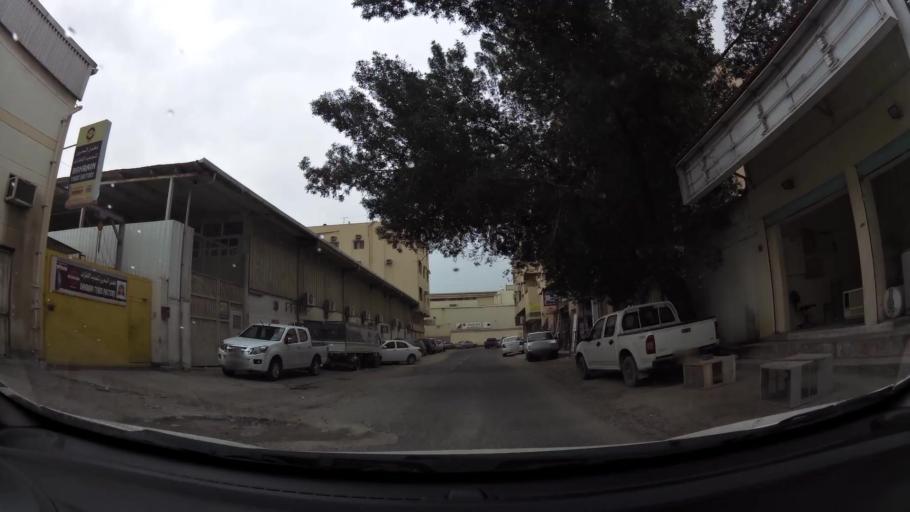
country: BH
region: Northern
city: Madinat `Isa
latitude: 26.1819
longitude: 50.5329
